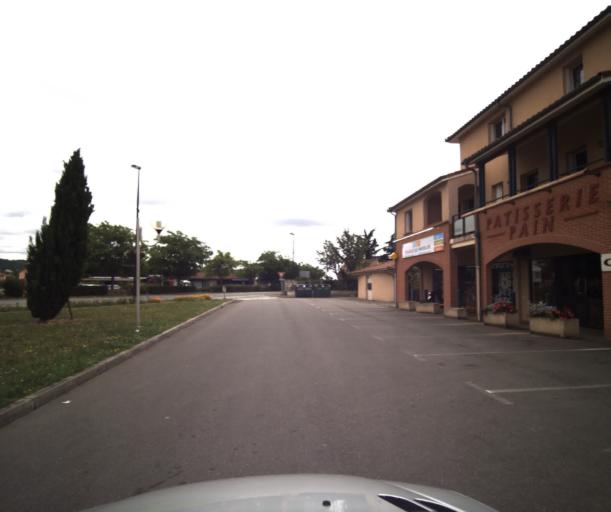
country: FR
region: Midi-Pyrenees
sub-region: Departement de la Haute-Garonne
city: Pinsaguel
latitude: 43.5017
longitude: 1.3916
